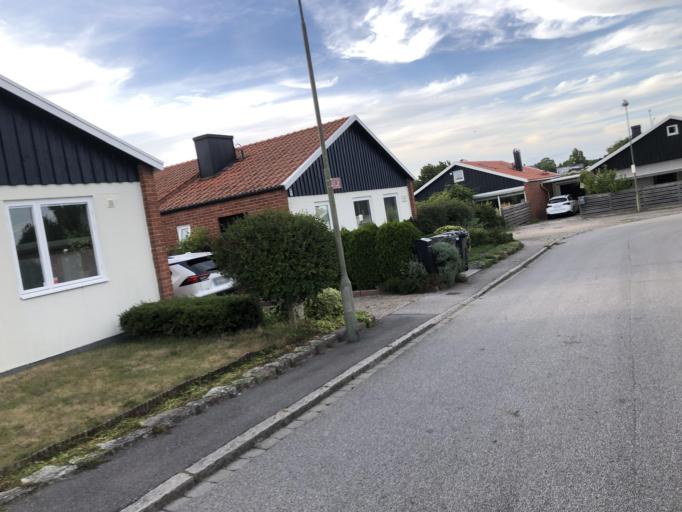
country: SE
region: Skane
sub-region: Burlovs Kommun
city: Arloev
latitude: 55.5937
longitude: 13.0752
